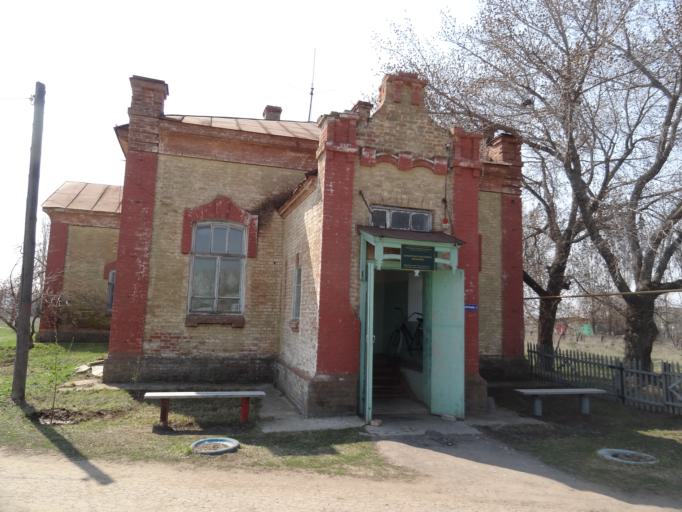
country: RU
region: Saratov
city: Privolzhskiy
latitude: 51.2512
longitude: 45.9257
